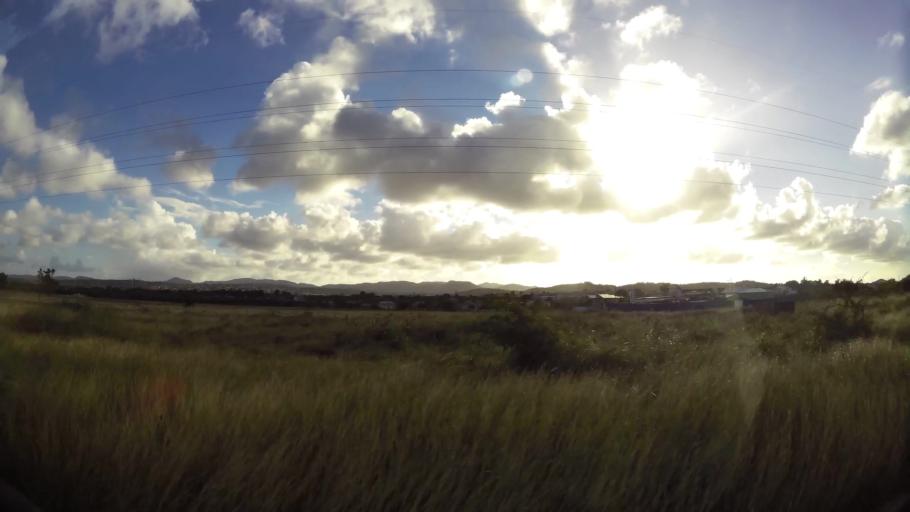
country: AG
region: Saint George
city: Piggotts
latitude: 17.1195
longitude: -61.7995
